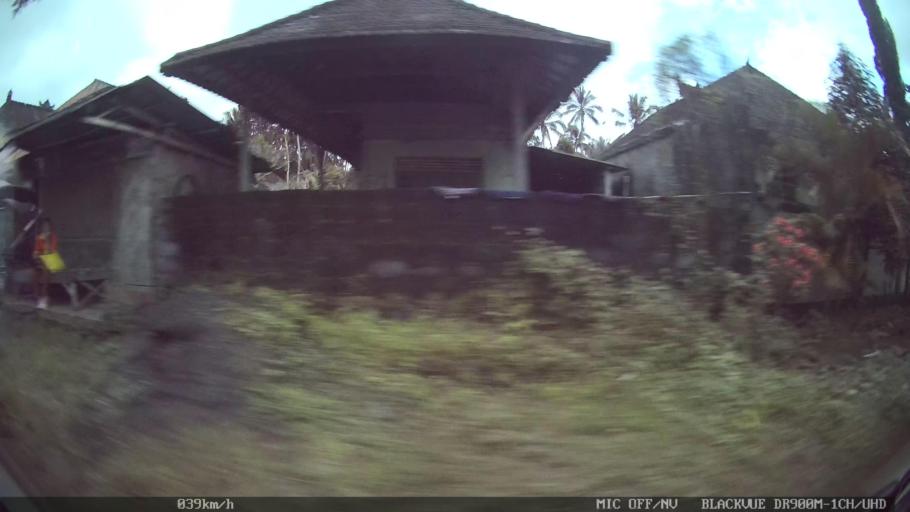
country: ID
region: Bali
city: Banjar Wangsian
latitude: -8.4467
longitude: 115.4238
